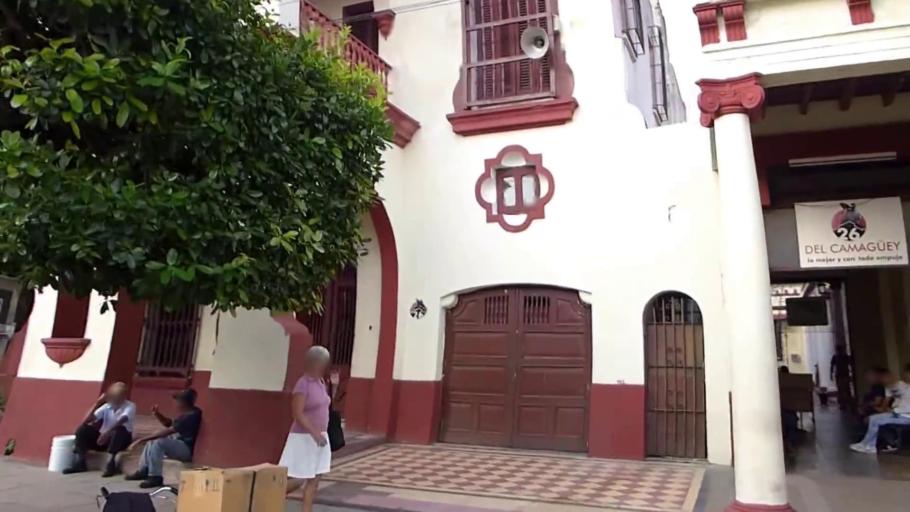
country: CU
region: Camaguey
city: Camaguey
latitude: 21.3734
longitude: -77.9115
